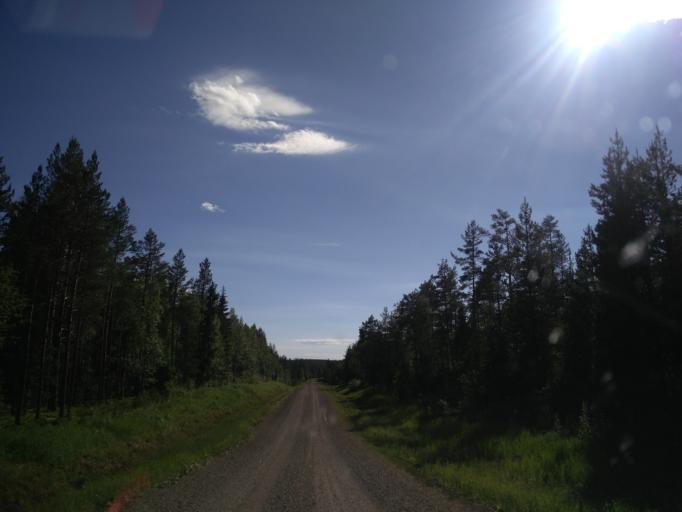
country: SE
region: Vaesternorrland
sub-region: Ange Kommun
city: Fransta
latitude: 62.2389
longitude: 16.3165
